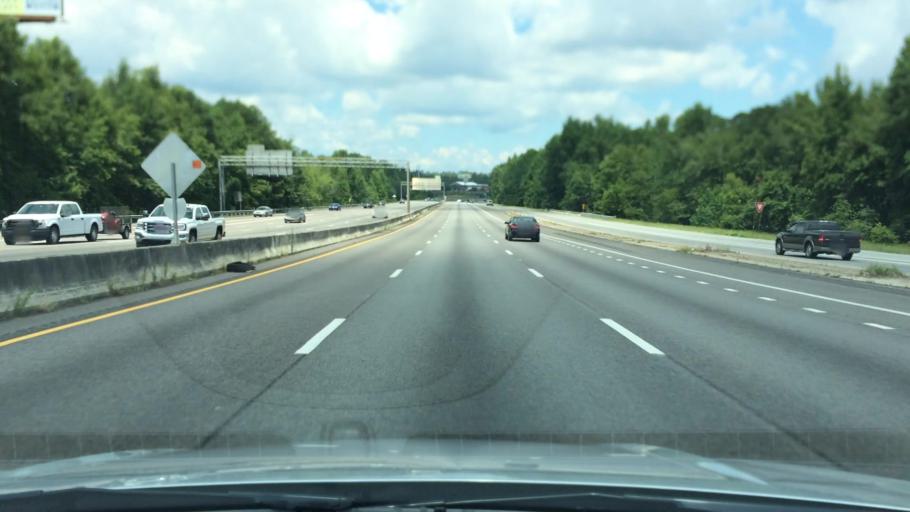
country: US
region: South Carolina
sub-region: Lexington County
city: Cayce
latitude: 33.9342
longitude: -81.0789
